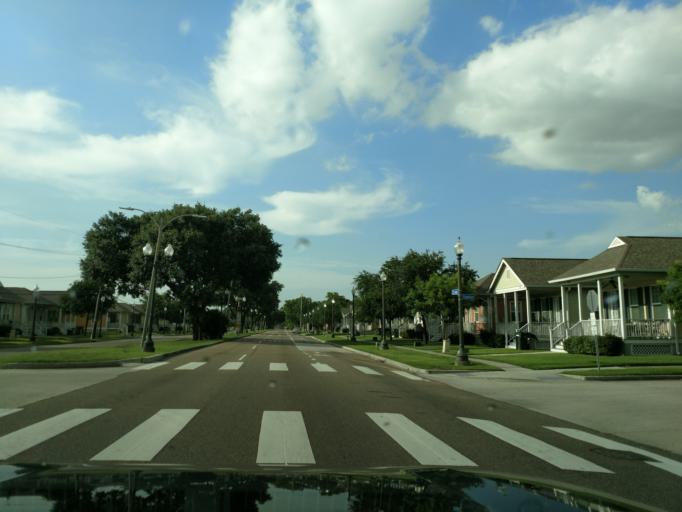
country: US
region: Louisiana
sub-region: Jefferson Parish
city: Gretna
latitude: 29.9321
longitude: -90.0416
